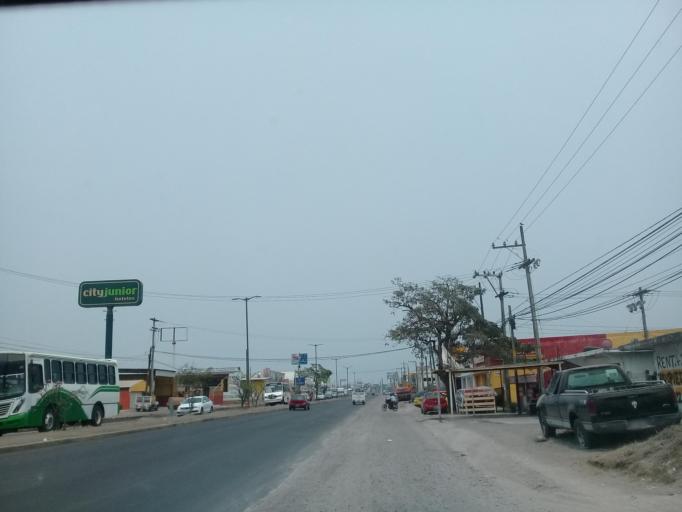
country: MX
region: Veracruz
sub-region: Veracruz
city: Las Amapolas
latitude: 19.1603
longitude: -96.2019
